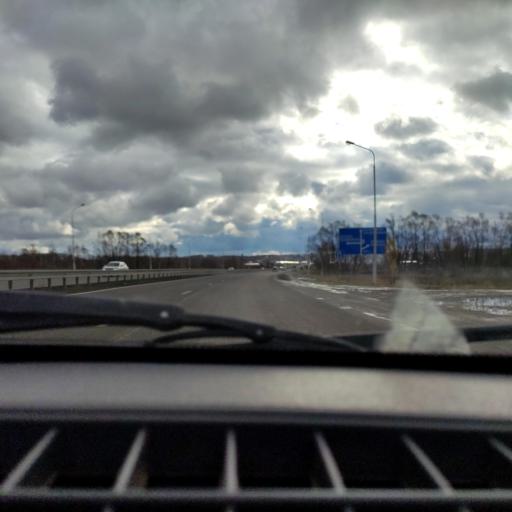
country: RU
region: Bashkortostan
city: Kabakovo
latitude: 54.6588
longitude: 56.0811
